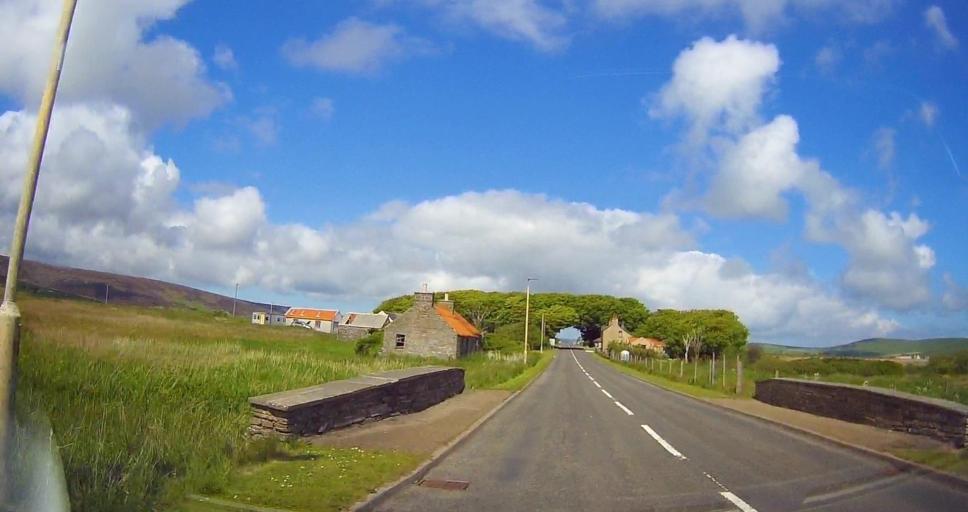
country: GB
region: Scotland
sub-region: Orkney Islands
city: Orkney
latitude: 59.0449
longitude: -3.0843
